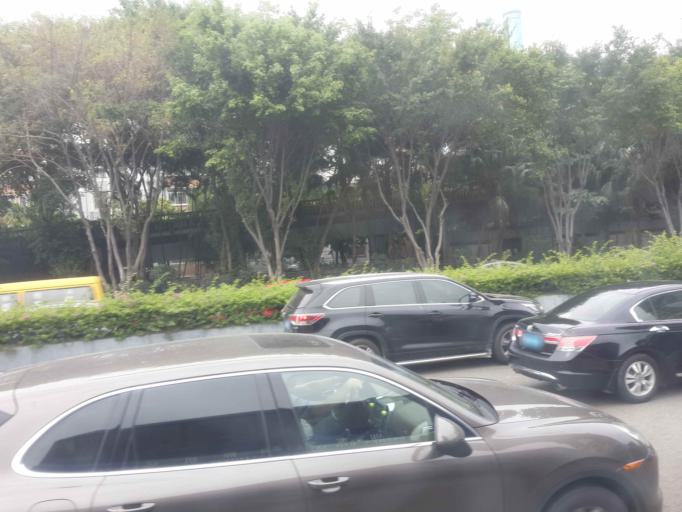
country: CN
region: Guangdong
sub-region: Shenzhen
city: Shenzhen
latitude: 22.5381
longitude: 114.1012
